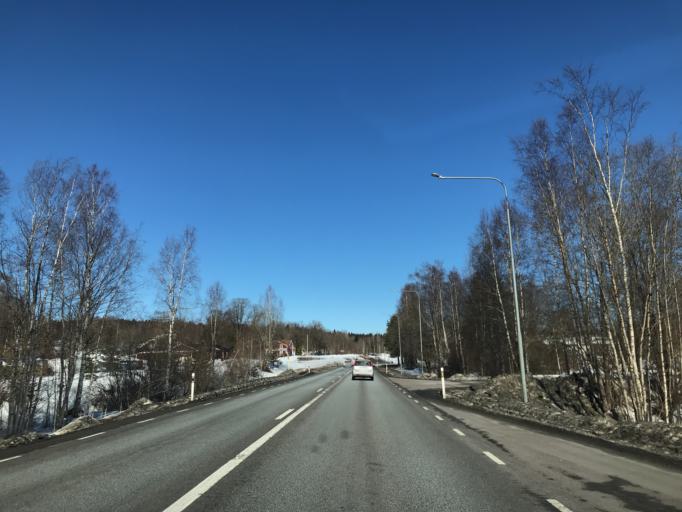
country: SE
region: Vaermland
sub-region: Filipstads Kommun
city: Filipstad
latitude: 59.7481
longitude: 14.2383
